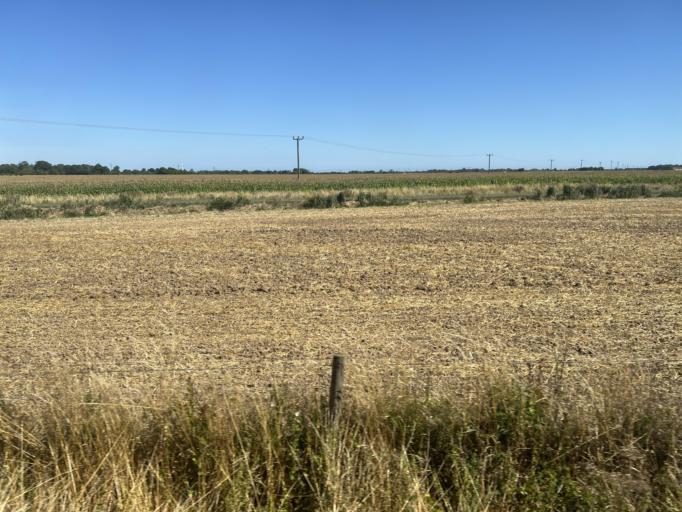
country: GB
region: England
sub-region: Lincolnshire
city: Wainfleet All Saints
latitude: 53.1144
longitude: 0.2147
